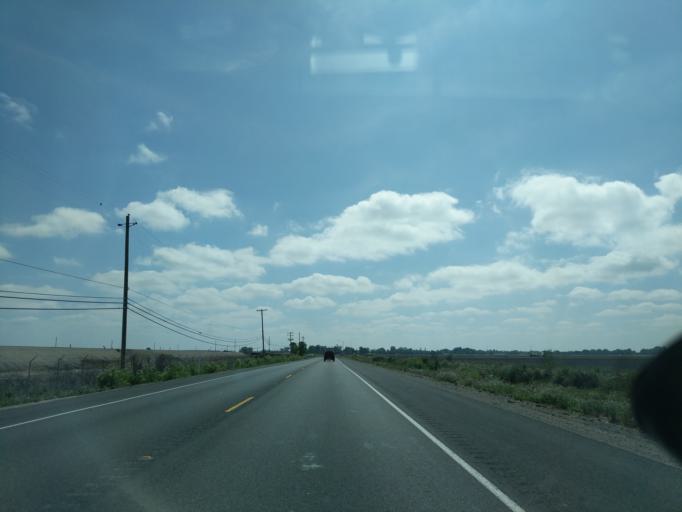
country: US
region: California
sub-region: San Joaquin County
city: Country Club
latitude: 37.9269
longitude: -121.3456
